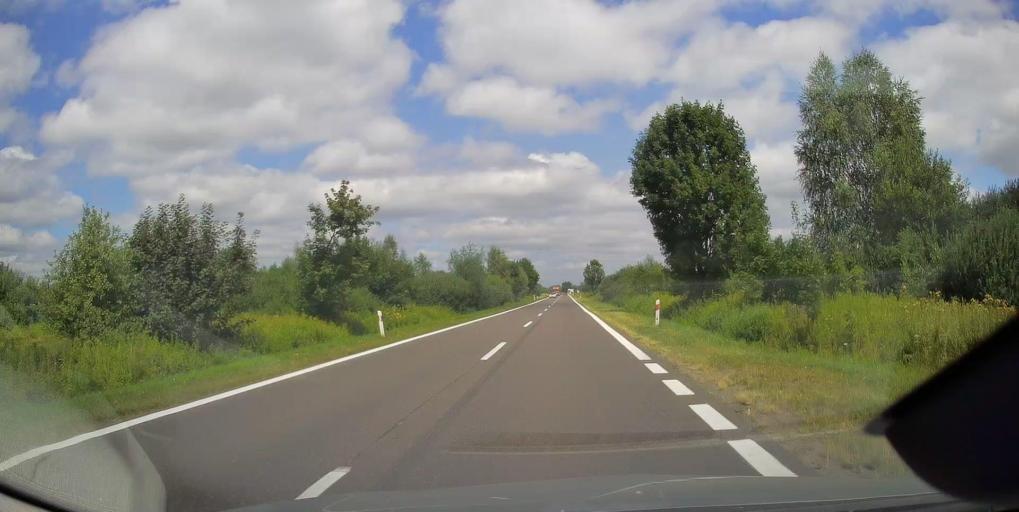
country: PL
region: Subcarpathian Voivodeship
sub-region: Powiat tarnobrzeski
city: Baranow Sandomierski
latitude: 50.4962
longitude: 21.5704
